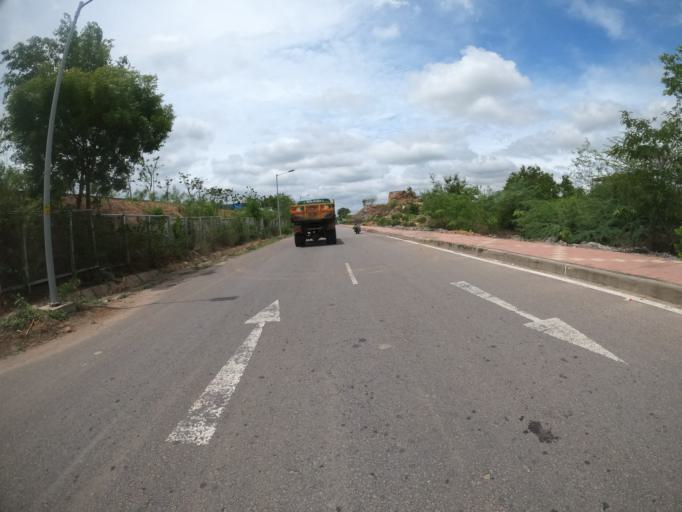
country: IN
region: Telangana
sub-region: Rangareddi
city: Balapur
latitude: 17.2737
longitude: 78.3807
